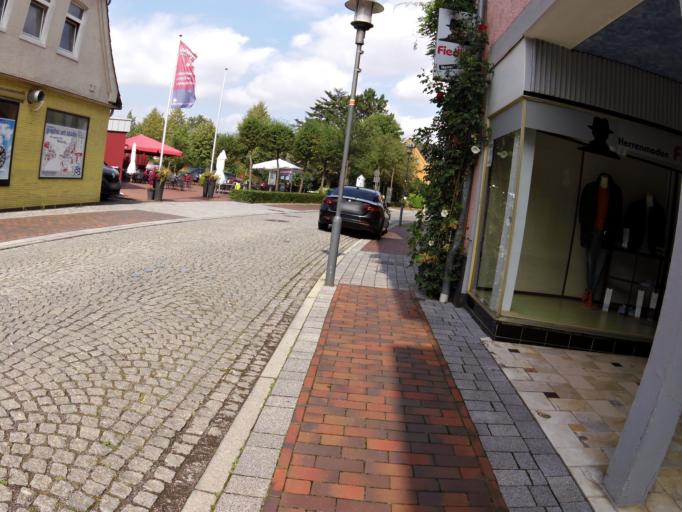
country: DE
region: Lower Saxony
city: Hoya
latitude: 52.8077
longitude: 9.1441
